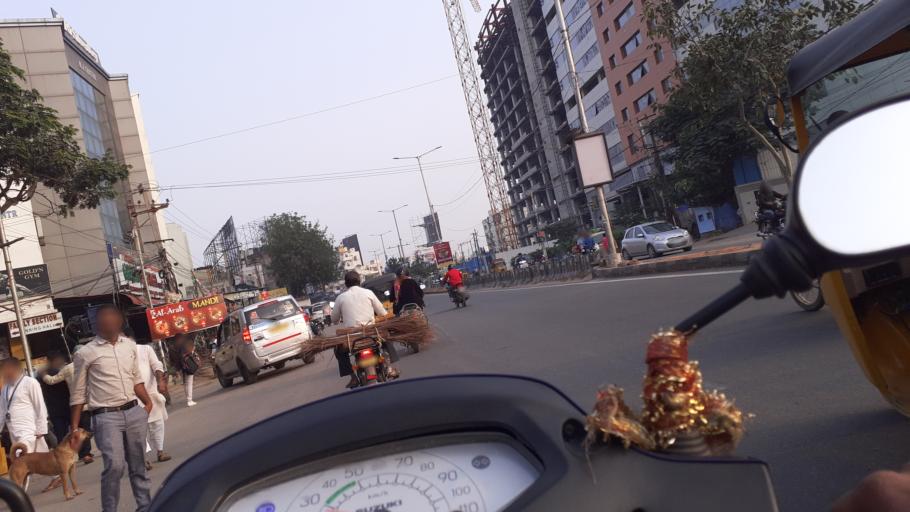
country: IN
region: Telangana
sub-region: Rangareddi
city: Kukatpalli
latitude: 17.4862
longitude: 78.3583
